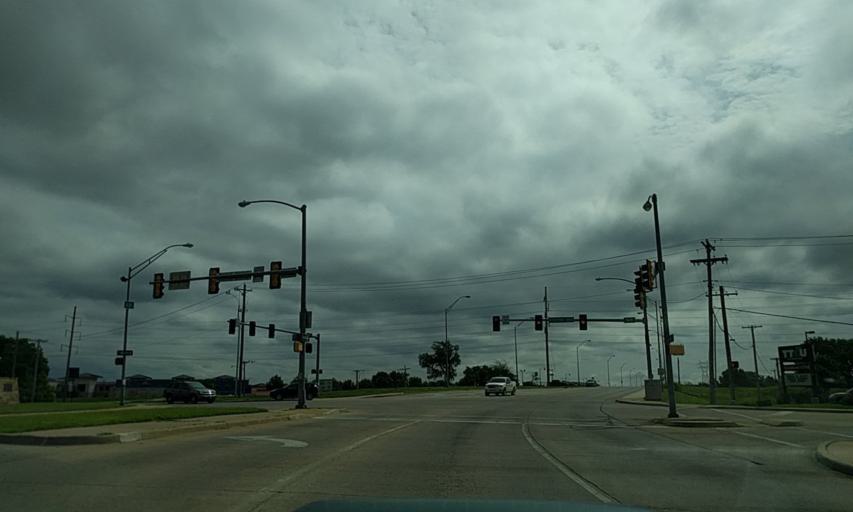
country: US
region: Oklahoma
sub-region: Tulsa County
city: Jenks
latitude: 36.0234
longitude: -95.9606
